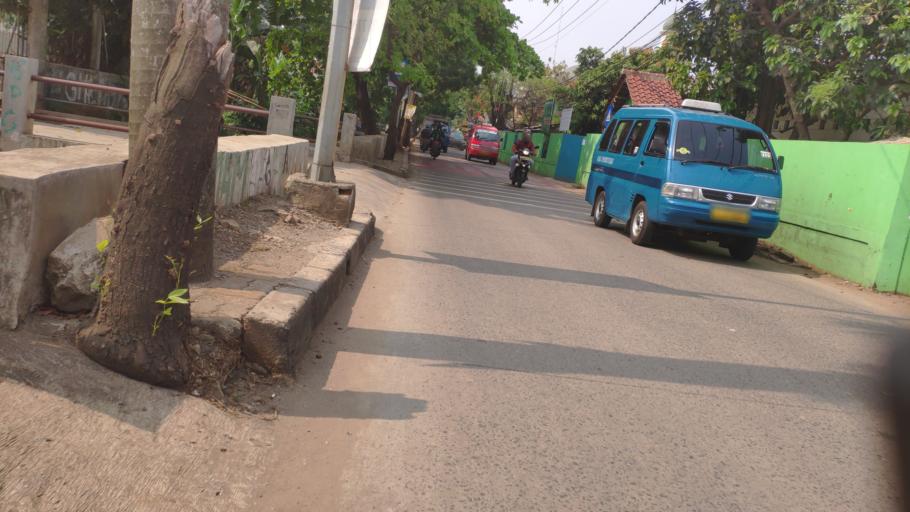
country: ID
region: West Java
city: Sawangan
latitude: -6.3810
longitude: 106.7904
